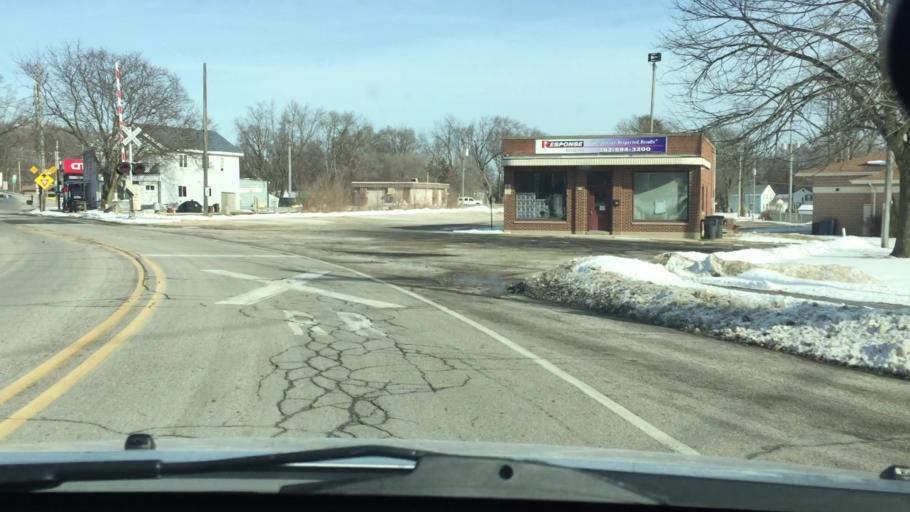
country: US
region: Wisconsin
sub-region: Waukesha County
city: Eagle
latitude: 42.8792
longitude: -88.4745
